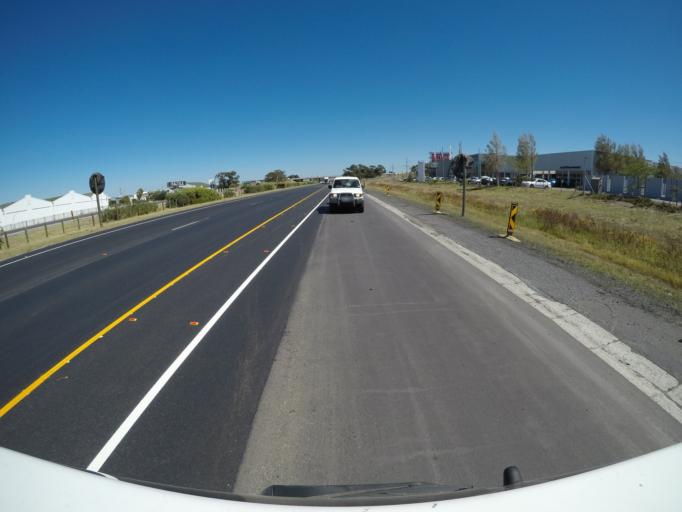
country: ZA
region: Western Cape
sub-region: Cape Winelands District Municipality
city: Stellenbosch
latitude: -34.0794
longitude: 18.8239
